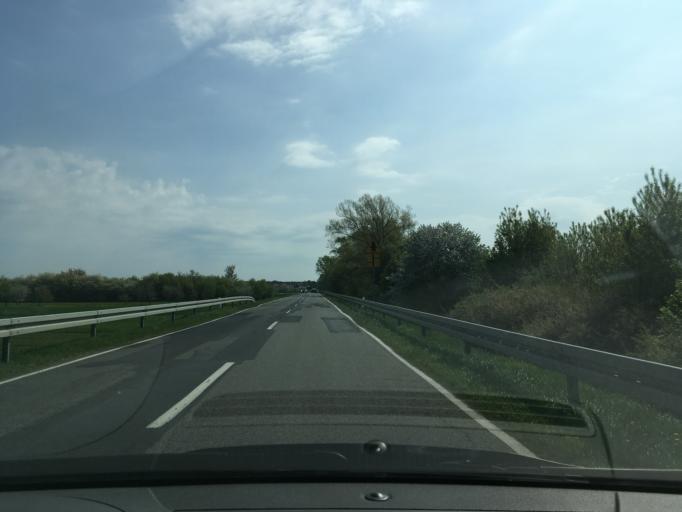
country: PL
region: Lublin Voivodeship
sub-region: Powiat rycki
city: Deblin
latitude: 51.4758
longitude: 21.8941
